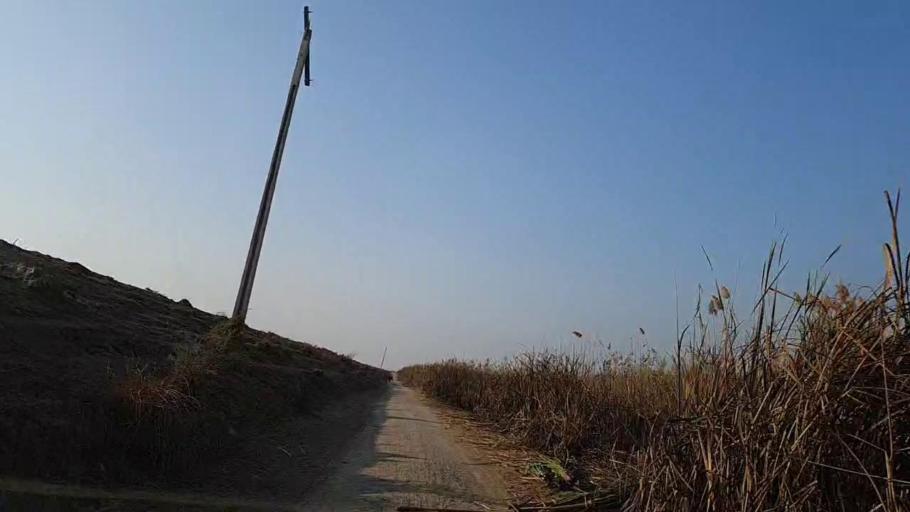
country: PK
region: Sindh
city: Sakrand
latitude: 26.0965
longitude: 68.3709
